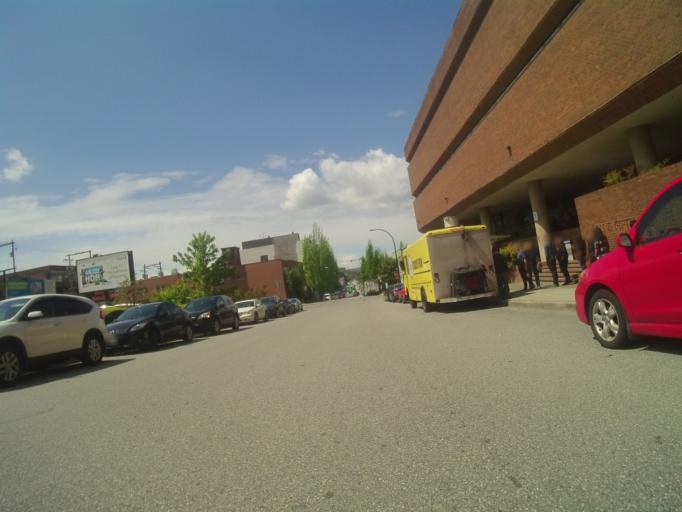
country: CA
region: British Columbia
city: Vancouver
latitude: 49.2664
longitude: -123.1019
